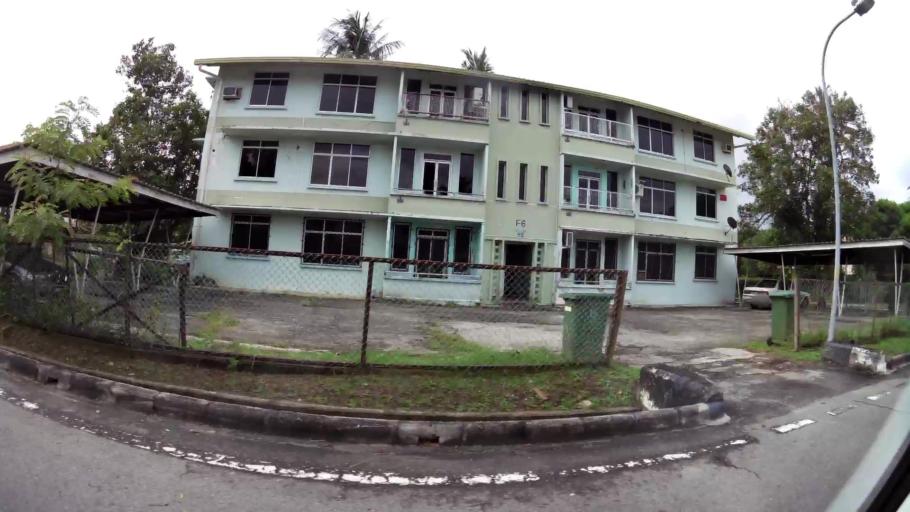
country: BN
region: Brunei and Muara
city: Bandar Seri Begawan
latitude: 4.9039
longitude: 114.9361
